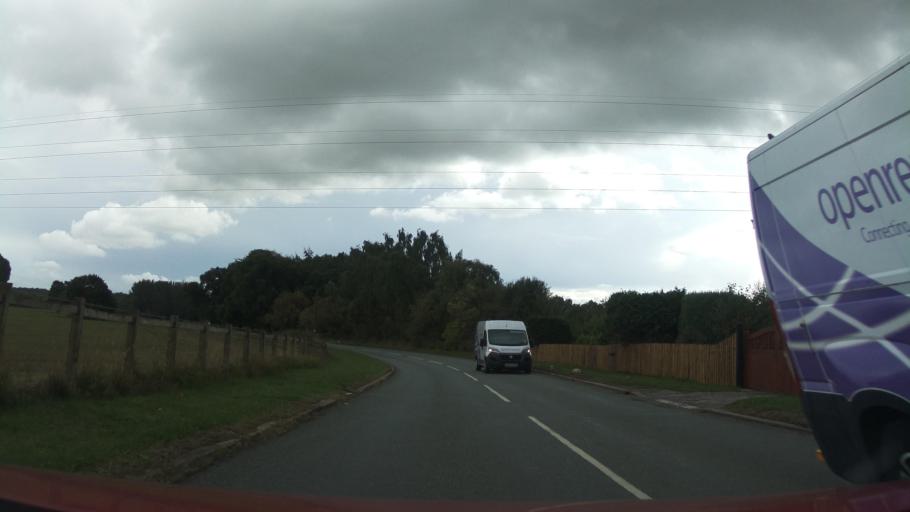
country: GB
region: England
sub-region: Staffordshire
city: Eccleshall
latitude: 52.9084
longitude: -2.2211
